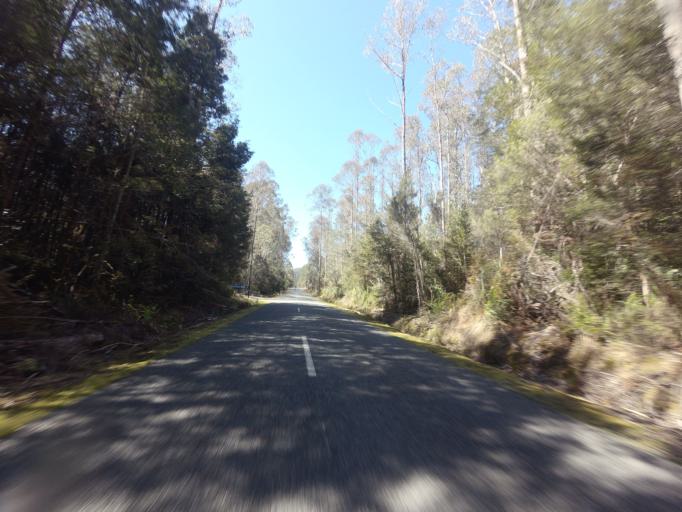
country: AU
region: Tasmania
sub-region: Derwent Valley
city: New Norfolk
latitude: -42.7428
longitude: 146.4172
